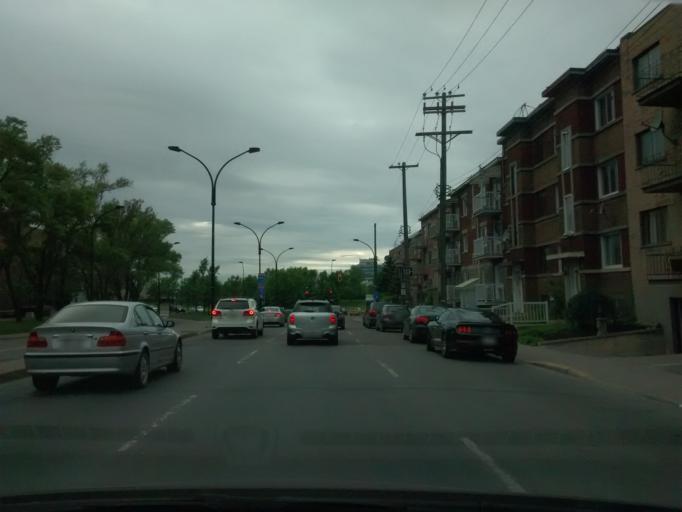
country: CA
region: Quebec
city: Mont-Royal
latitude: 45.5300
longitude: -73.6457
